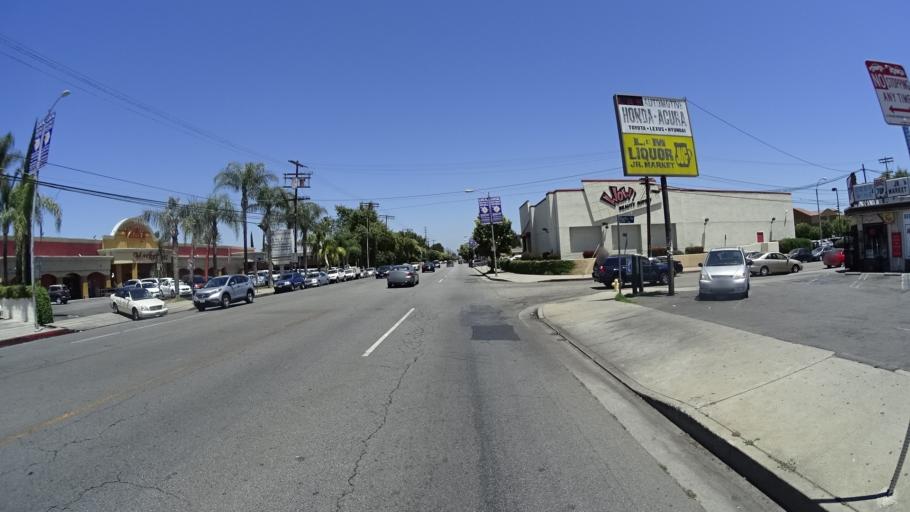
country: US
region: California
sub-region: Los Angeles County
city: Northridge
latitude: 34.1937
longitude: -118.5339
